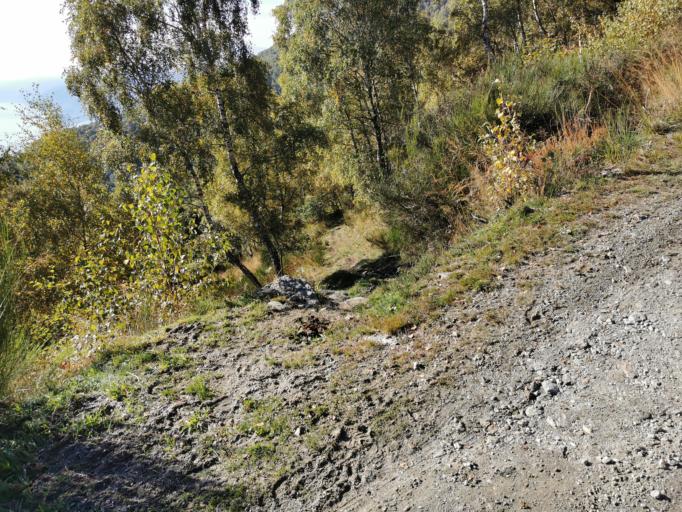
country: IT
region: Lombardy
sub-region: Provincia di Como
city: Cremia
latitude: 46.0857
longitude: 9.2482
